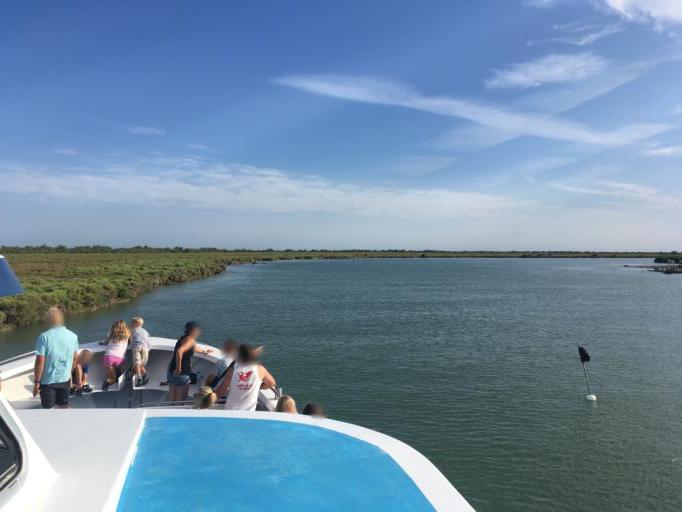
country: FR
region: Provence-Alpes-Cote d'Azur
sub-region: Departement des Bouches-du-Rhone
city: Saintes-Maries-de-la-Mer
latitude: 43.4686
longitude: 4.3896
